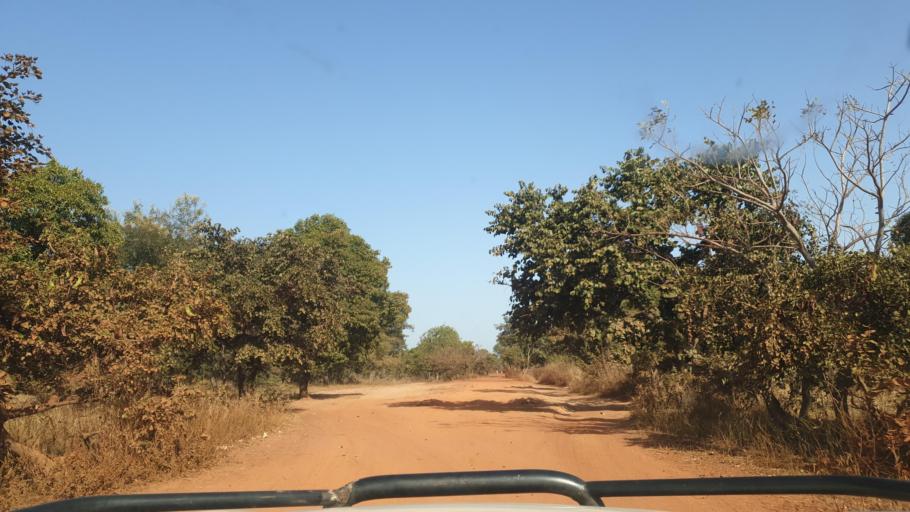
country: ML
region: Sikasso
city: Kolondieba
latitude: 11.7387
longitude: -6.8945
